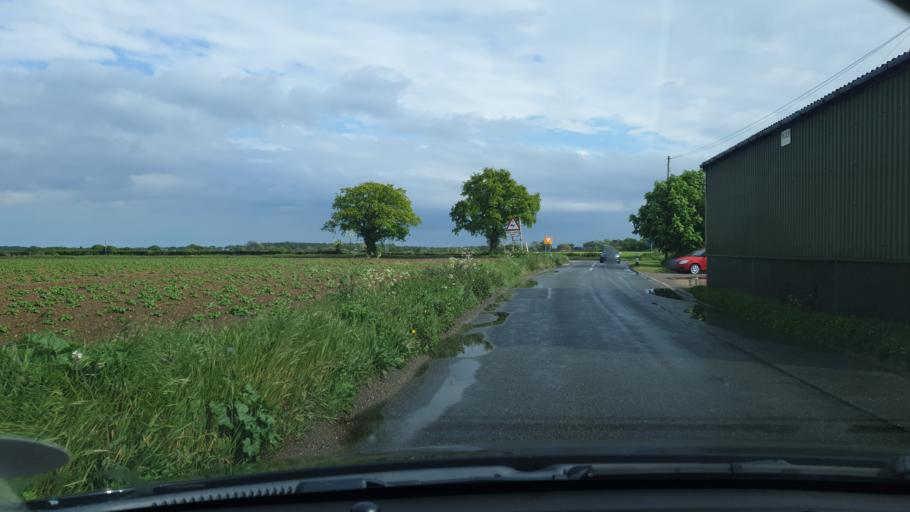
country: GB
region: England
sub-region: Essex
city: Great Bentley
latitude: 51.8526
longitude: 1.0431
